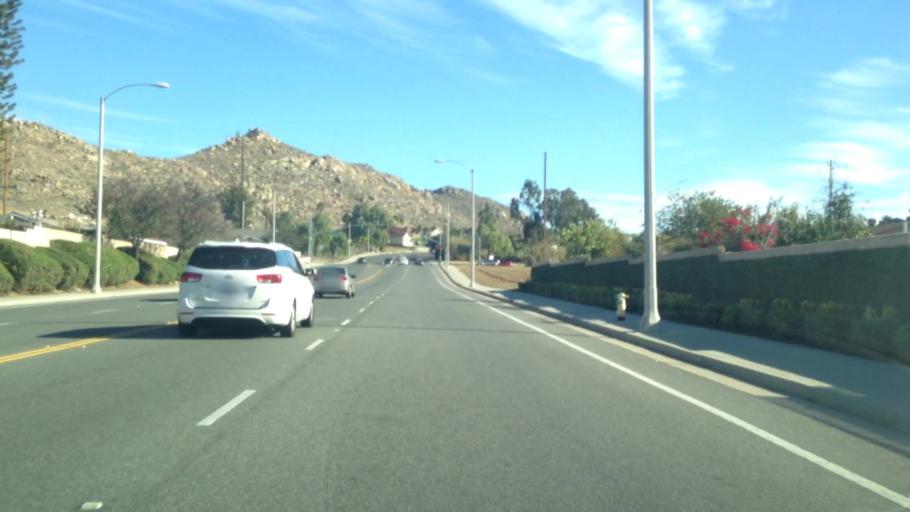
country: US
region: California
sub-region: Riverside County
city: Pedley
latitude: 33.9196
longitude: -117.4701
